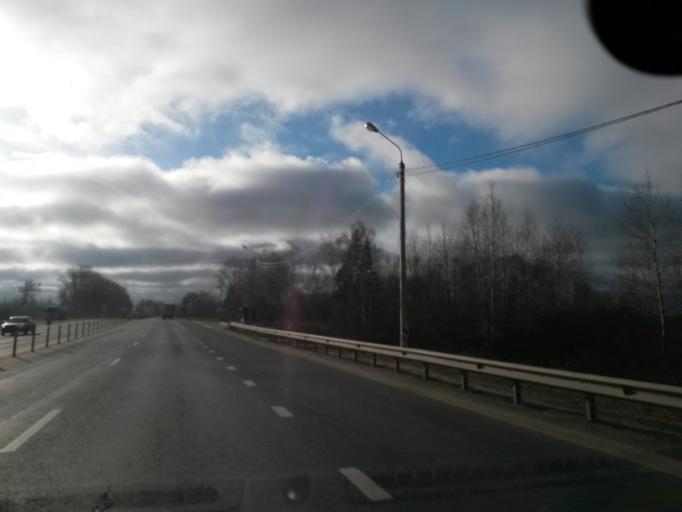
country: RU
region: Jaroslavl
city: Semibratovo
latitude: 57.3443
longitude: 39.5823
